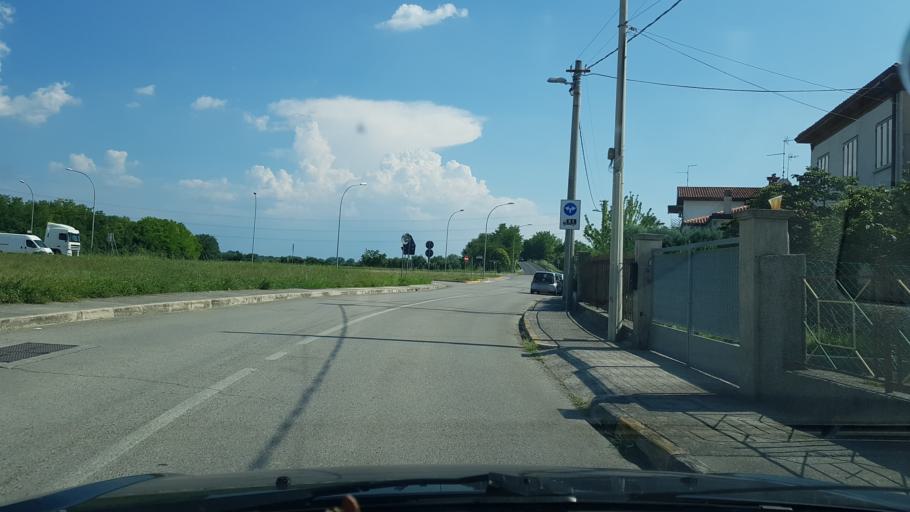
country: IT
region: Friuli Venezia Giulia
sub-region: Provincia di Gorizia
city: Staranzano
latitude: 45.7928
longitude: 13.5052
